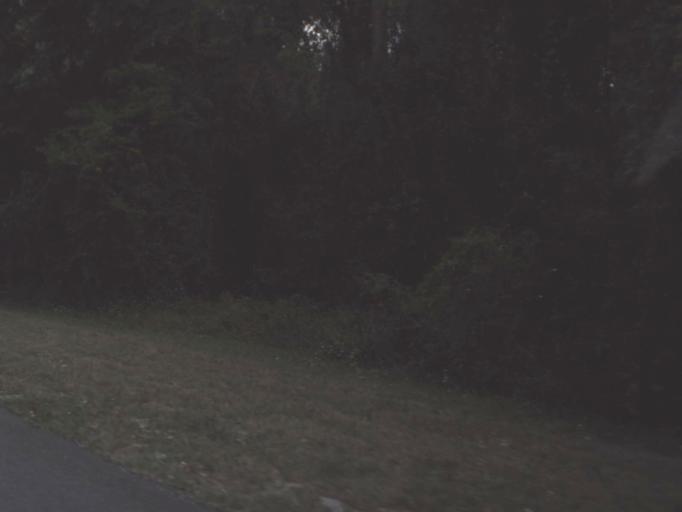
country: US
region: Florida
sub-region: Hernando County
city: Ridge Manor
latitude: 28.5401
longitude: -82.0909
